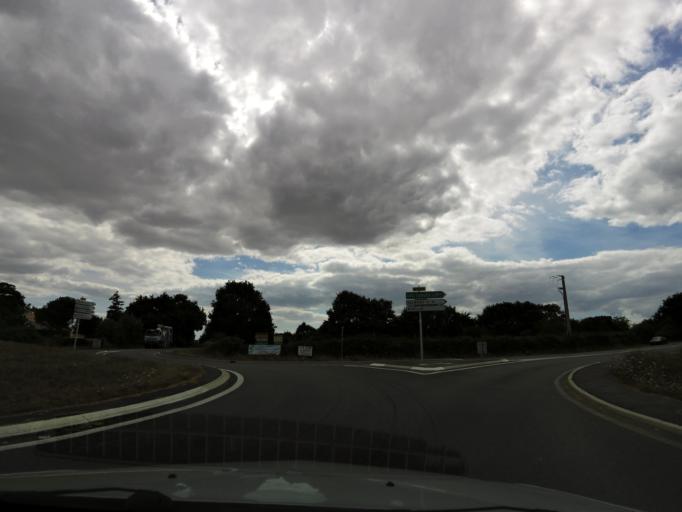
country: FR
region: Pays de la Loire
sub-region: Departement de la Vendee
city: Avrille
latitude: 46.4622
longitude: -1.4551
